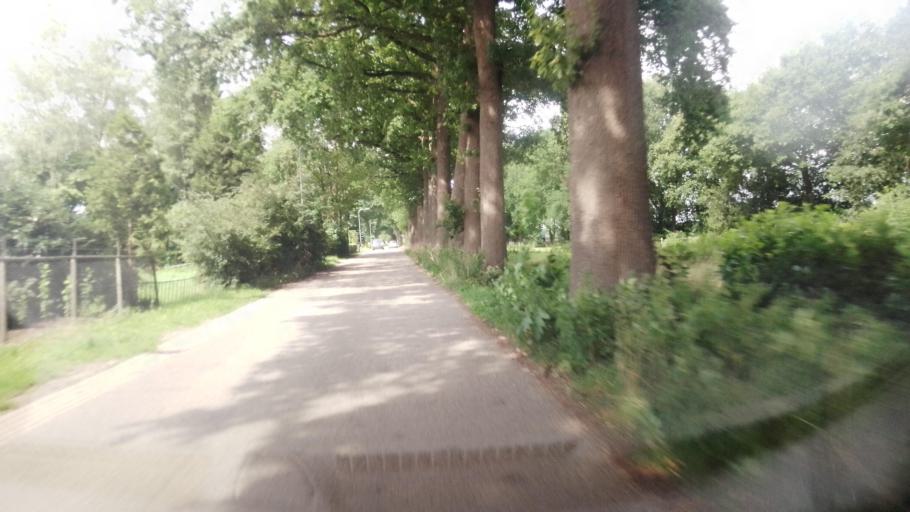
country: NL
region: Limburg
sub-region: Gemeente Venray
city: Venray
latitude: 51.4447
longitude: 5.8872
